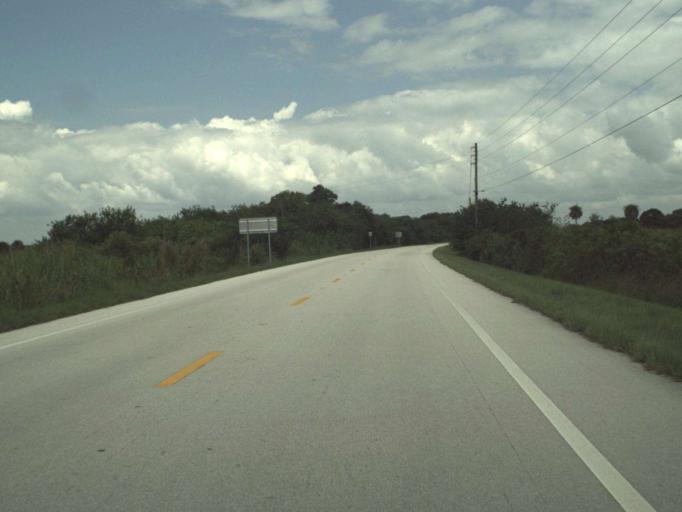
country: US
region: Florida
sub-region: Okeechobee County
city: Taylor Creek
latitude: 27.1206
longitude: -80.6752
